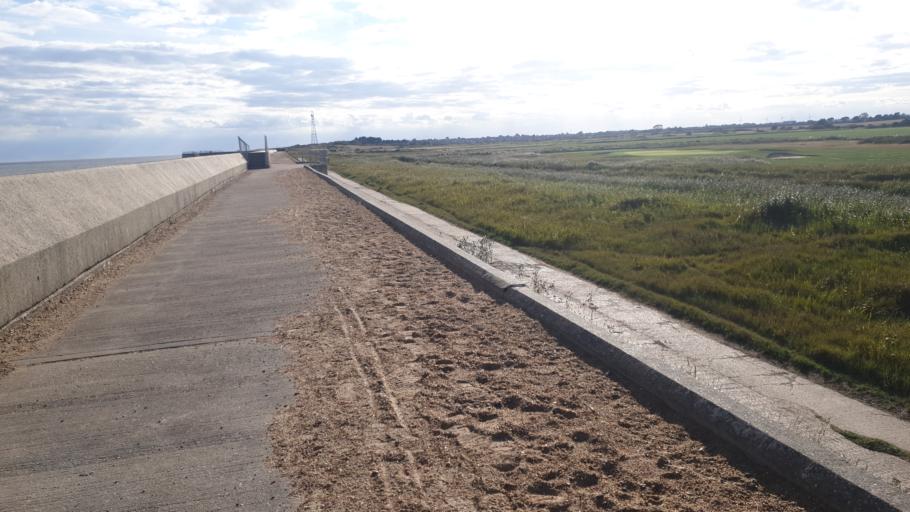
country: GB
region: England
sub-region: Essex
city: Frinton-on-Sea
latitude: 51.8162
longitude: 1.2299
